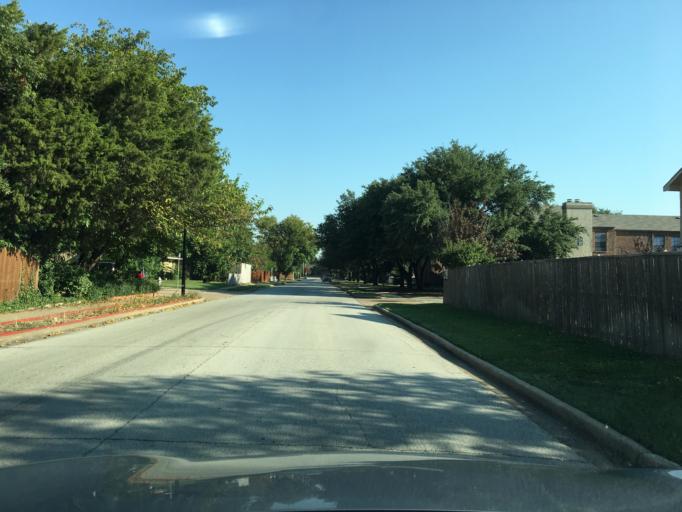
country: US
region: Texas
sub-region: Dallas County
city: Garland
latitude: 32.9488
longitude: -96.6561
